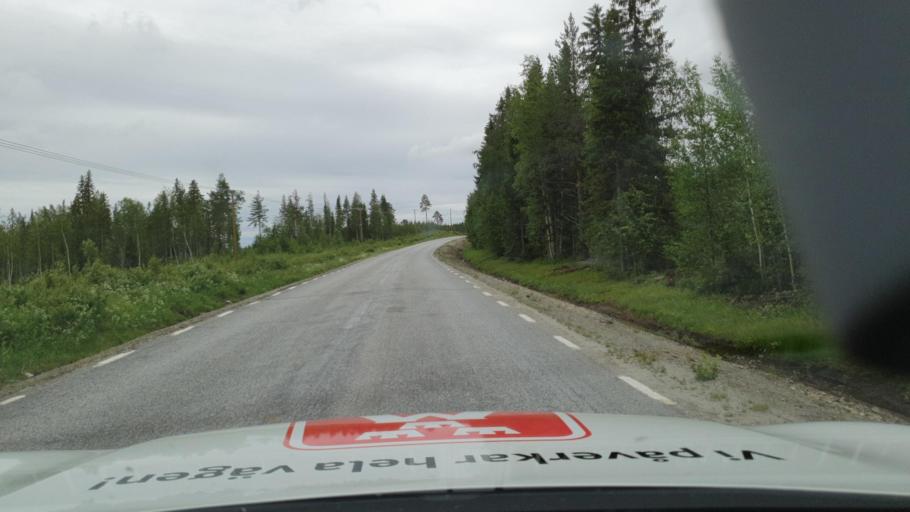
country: SE
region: Vaesterbotten
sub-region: Lycksele Kommun
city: Lycksele
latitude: 64.1451
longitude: 18.3608
